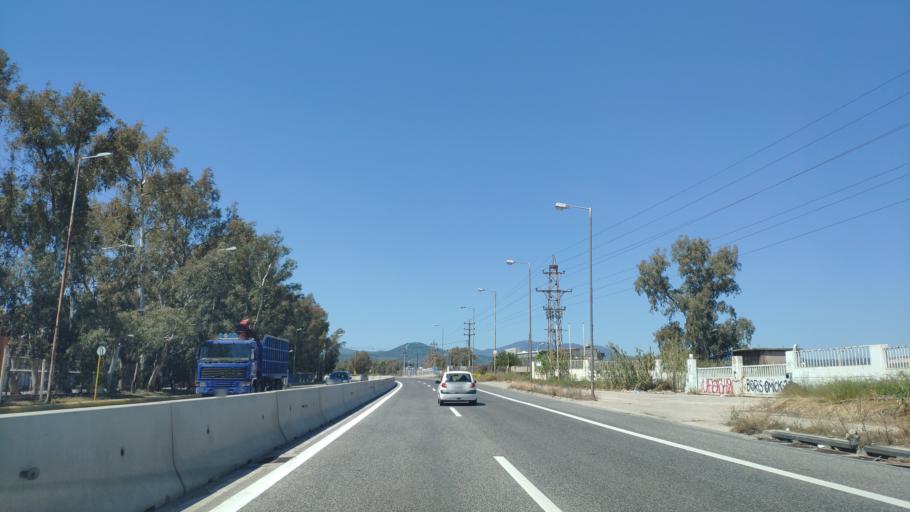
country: GR
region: Attica
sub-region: Nomarchia Dytikis Attikis
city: Elefsina
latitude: 38.0501
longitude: 23.5627
